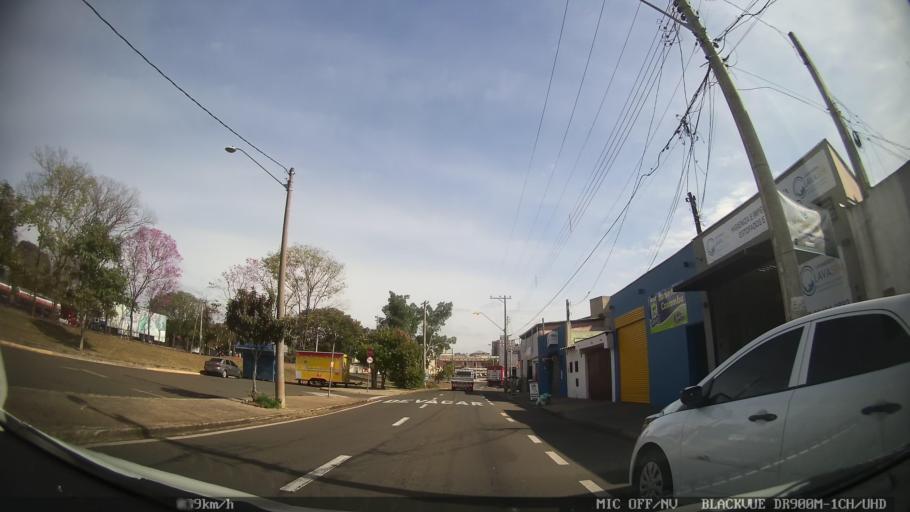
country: BR
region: Sao Paulo
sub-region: Piracicaba
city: Piracicaba
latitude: -22.7475
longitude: -47.6329
